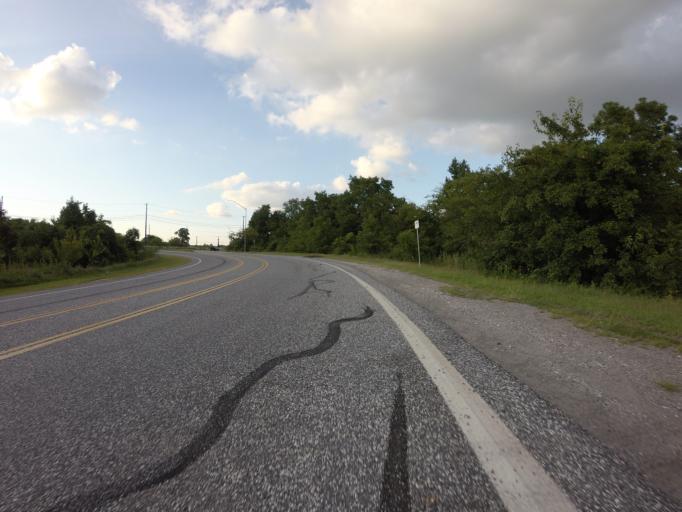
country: US
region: Maryland
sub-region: Baltimore County
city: Edgemere
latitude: 39.2307
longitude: -76.4633
